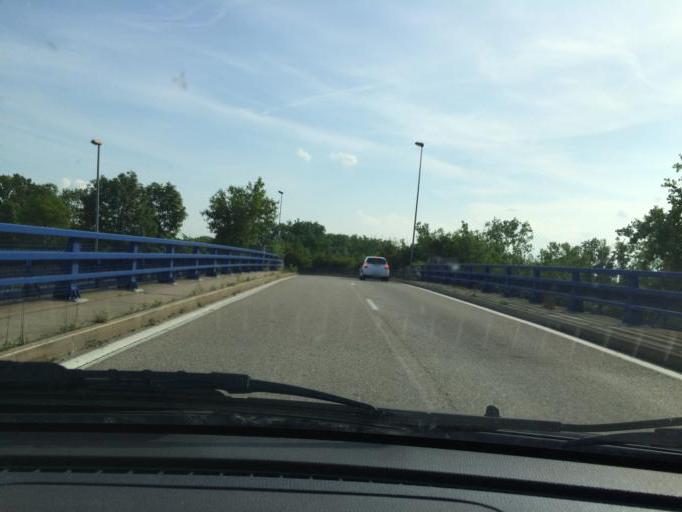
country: FR
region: Rhone-Alpes
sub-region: Departement du Rhone
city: Villeurbanne
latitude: 45.7907
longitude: 4.8844
